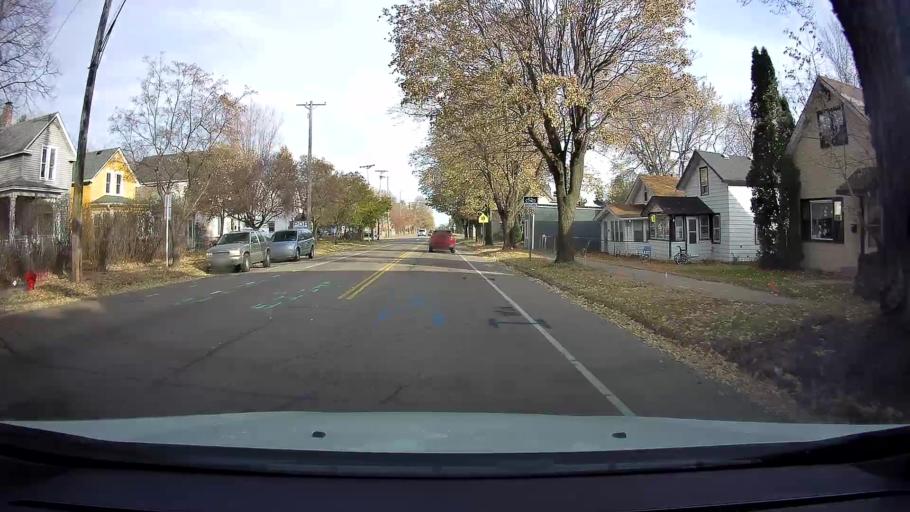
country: US
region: Minnesota
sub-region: Ramsey County
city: Falcon Heights
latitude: 44.9702
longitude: -93.1429
